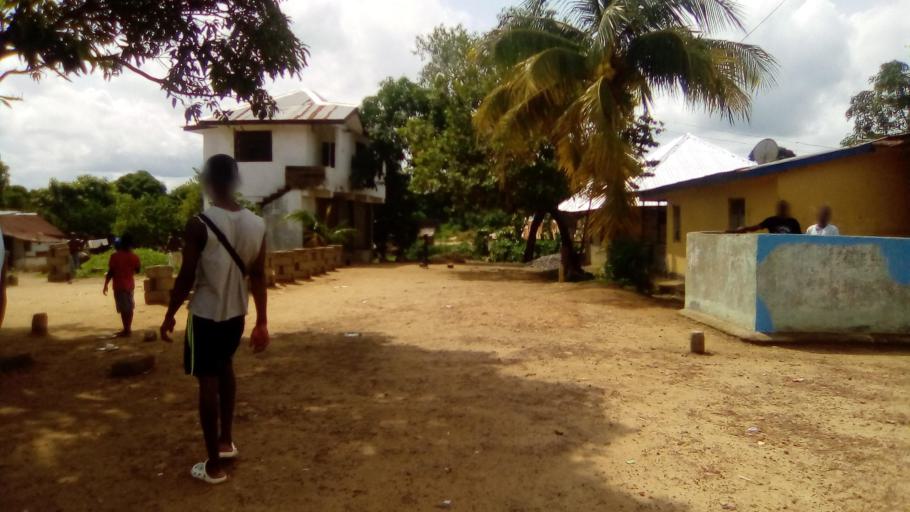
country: SL
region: Southern Province
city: Bo
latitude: 7.9788
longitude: -11.7433
